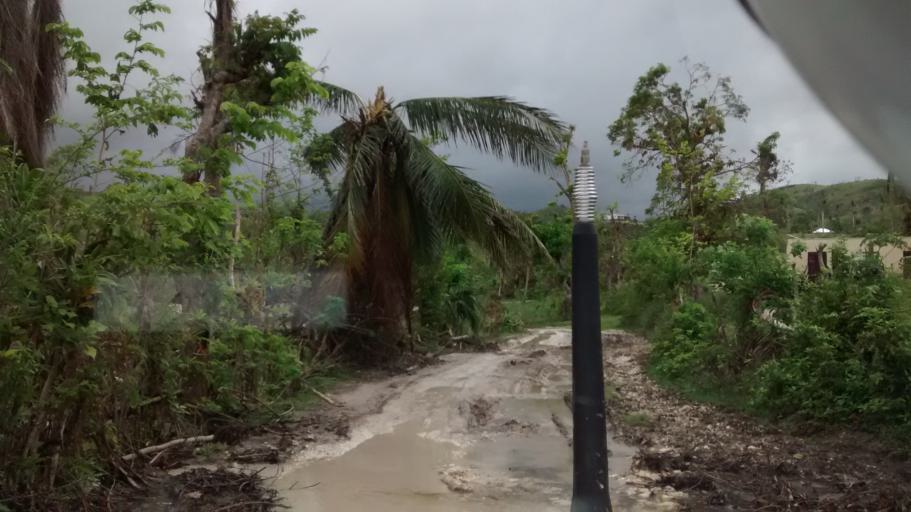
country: HT
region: Grandans
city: Jeremie
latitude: 18.5711
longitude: -74.1521
